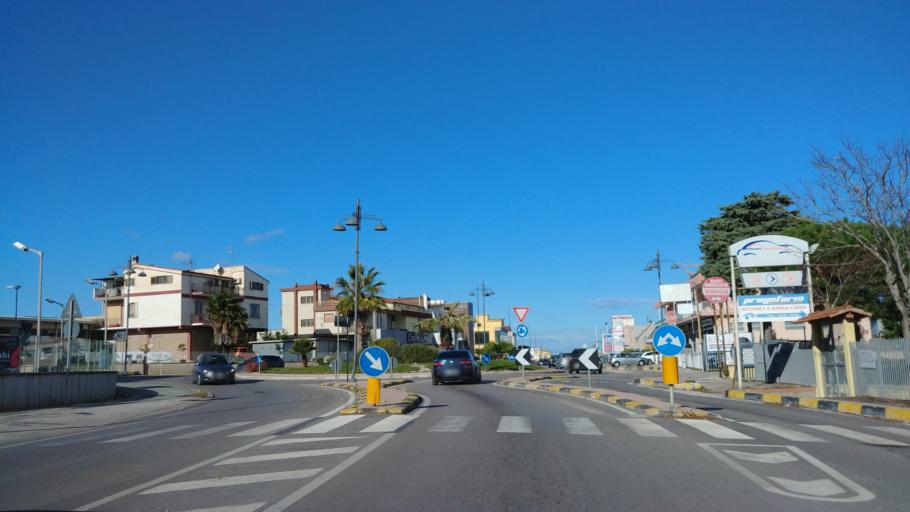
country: IT
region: Molise
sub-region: Provincia di Campobasso
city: Termoli
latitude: 41.9859
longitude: 15.0036
